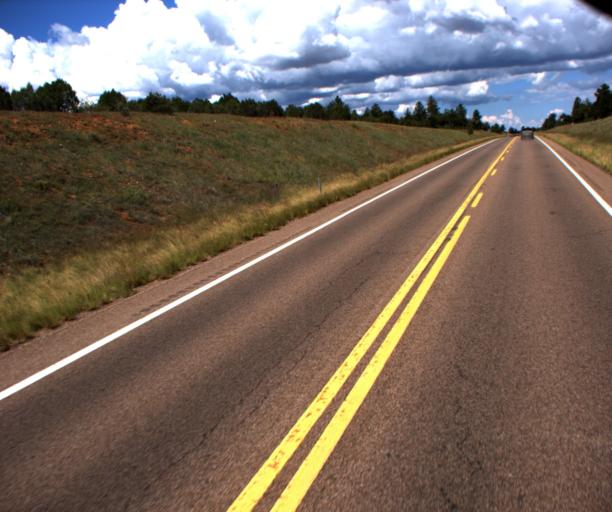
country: US
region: Arizona
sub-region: Navajo County
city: Heber-Overgaard
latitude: 34.3743
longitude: -110.4615
